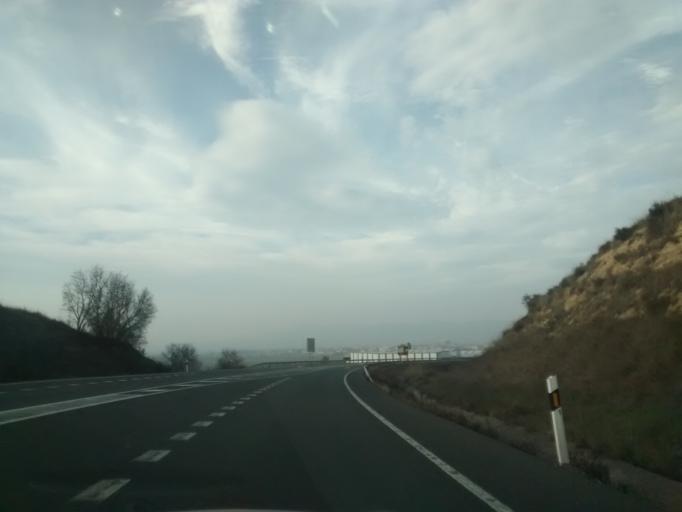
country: ES
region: La Rioja
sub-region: Provincia de La Rioja
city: Ollauri
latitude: 42.5493
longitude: -2.8321
